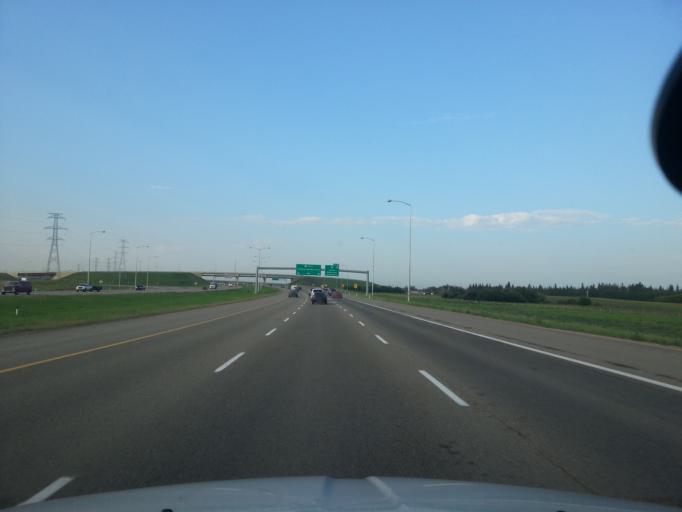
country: CA
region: Alberta
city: St. Albert
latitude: 53.5824
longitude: -113.6578
